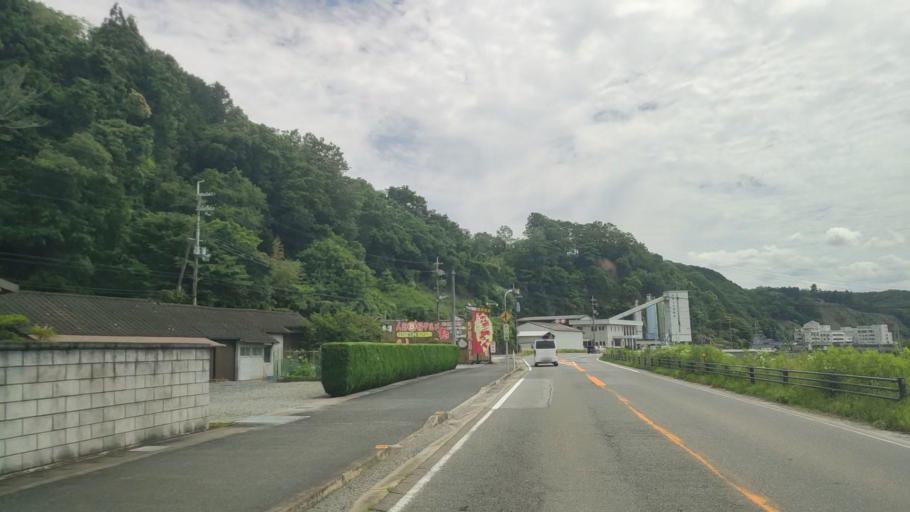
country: JP
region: Hyogo
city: Yamazakicho-nakabirose
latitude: 35.0142
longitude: 134.3696
